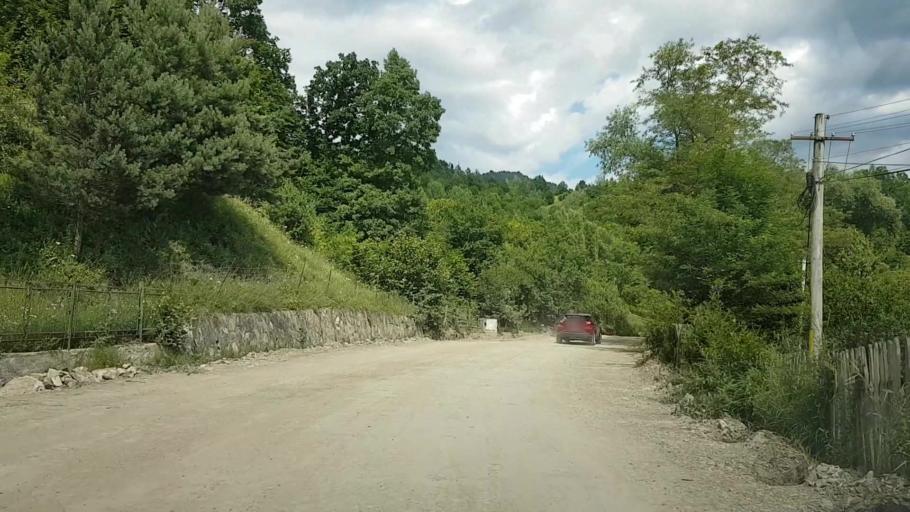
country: RO
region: Neamt
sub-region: Comuna Hangu
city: Hangu
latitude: 47.0473
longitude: 26.0471
